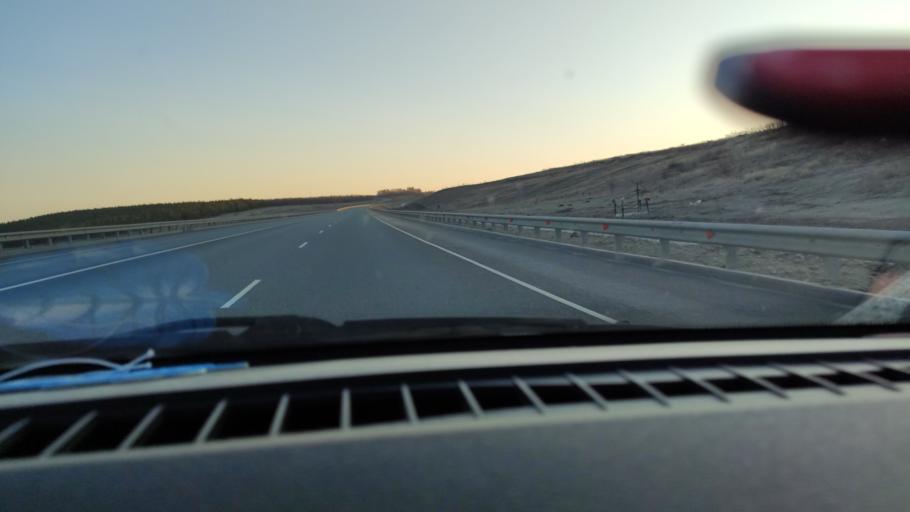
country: RU
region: Saratov
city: Yelshanka
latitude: 51.8752
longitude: 46.5061
